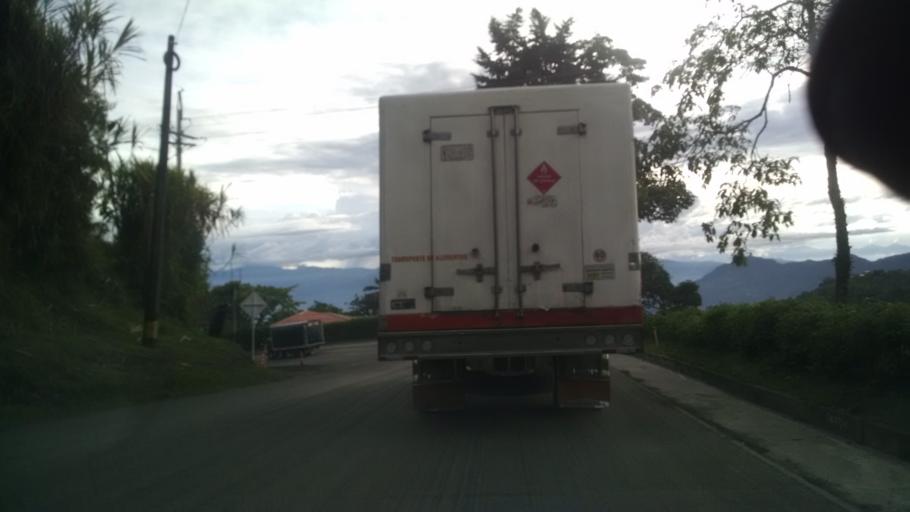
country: CO
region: Antioquia
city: Santa Barbara
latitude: 5.9096
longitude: -75.5750
